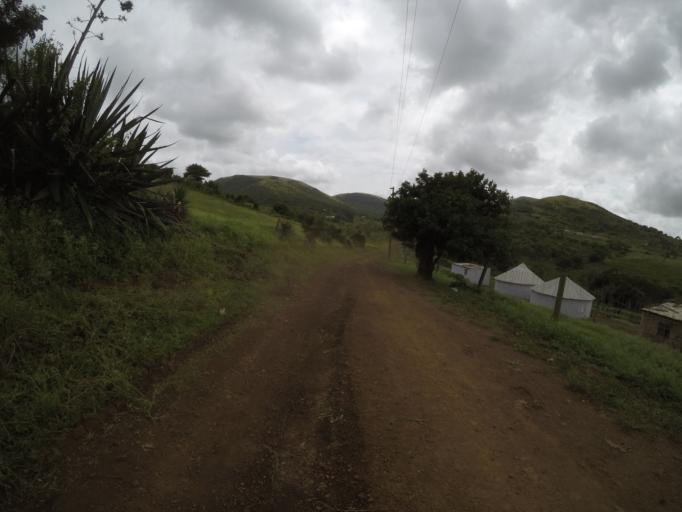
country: ZA
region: KwaZulu-Natal
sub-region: uThungulu District Municipality
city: Empangeni
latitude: -28.5873
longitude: 31.8887
